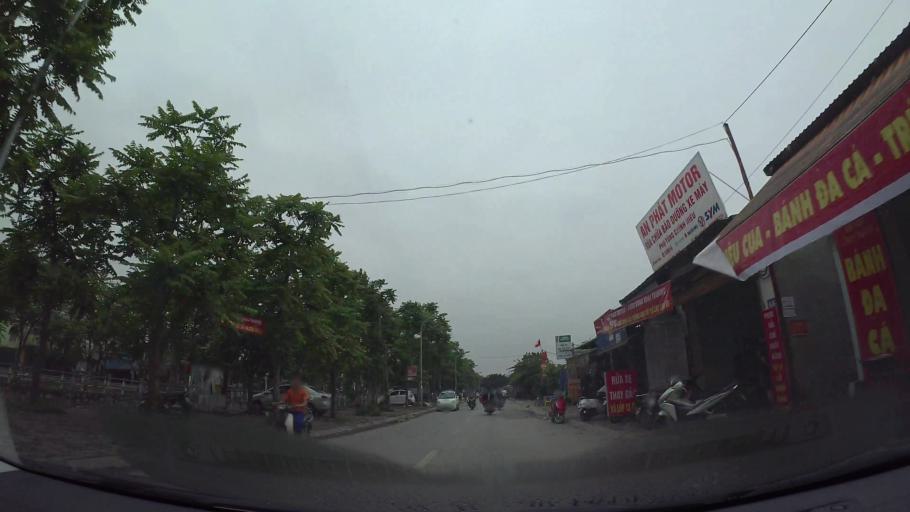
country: VN
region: Ha Noi
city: Hai BaTrung
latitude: 20.9914
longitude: 105.8732
